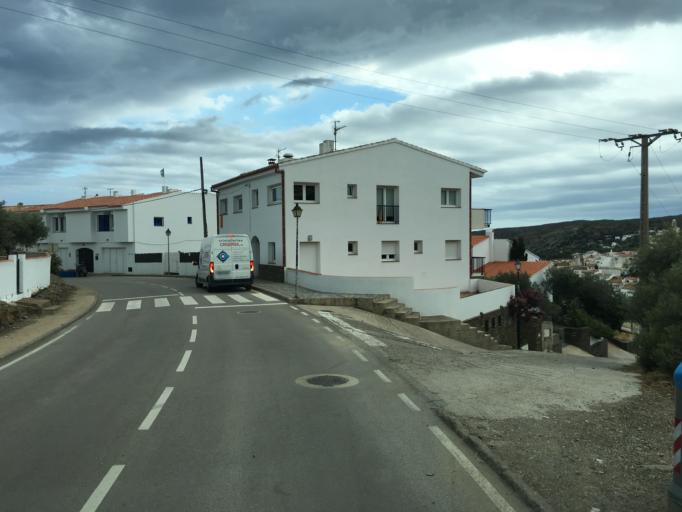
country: ES
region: Catalonia
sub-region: Provincia de Girona
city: Cadaques
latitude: 42.2925
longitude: 3.2756
